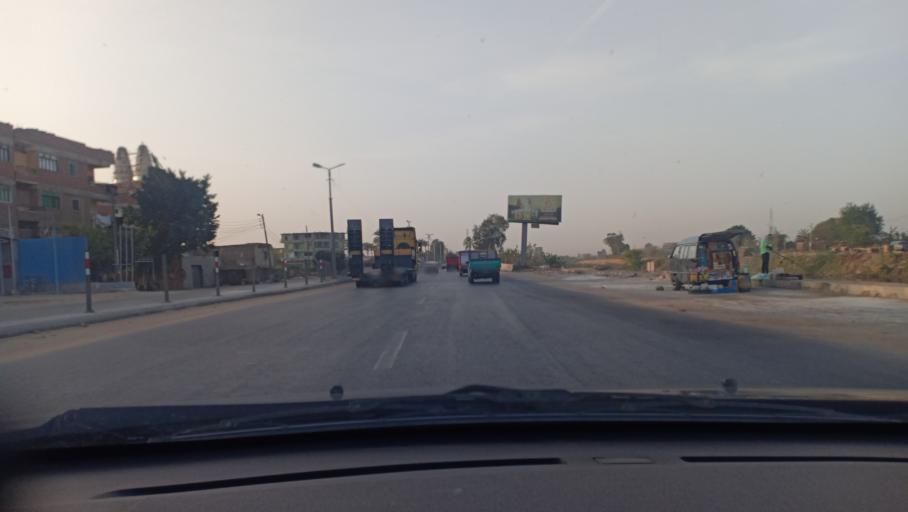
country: EG
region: Muhafazat al Minufiyah
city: Quwaysina
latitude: 30.5528
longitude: 31.2685
